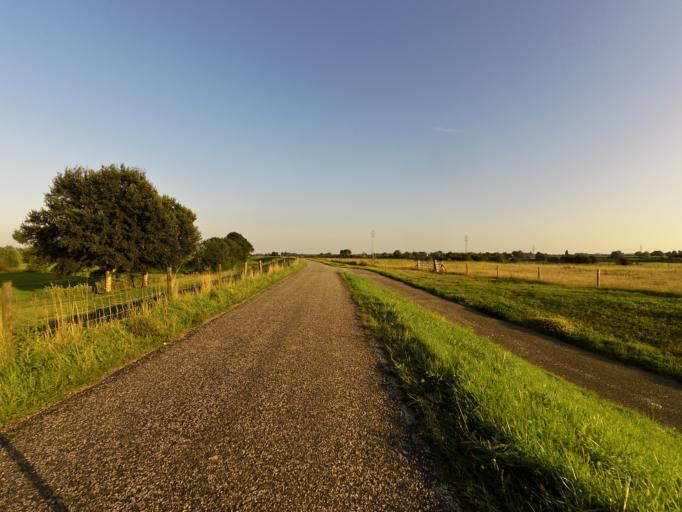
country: NL
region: Gelderland
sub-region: Gemeente Duiven
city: Duiven
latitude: 51.9130
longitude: 5.9979
